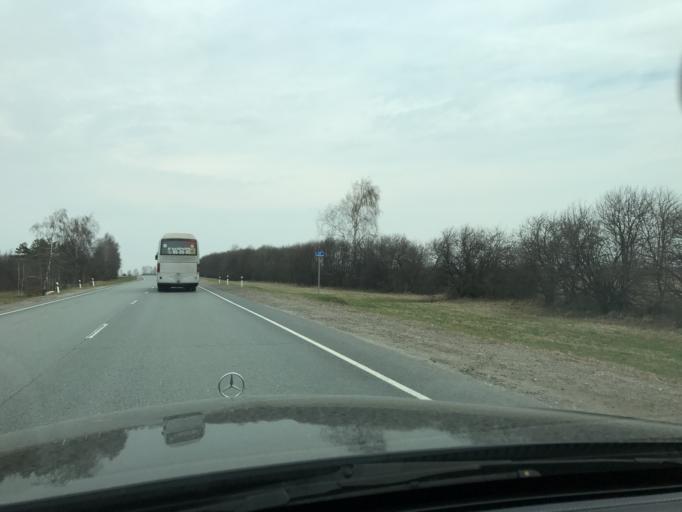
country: RU
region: Vladimir
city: Suzdal'
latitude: 56.3513
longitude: 40.4731
